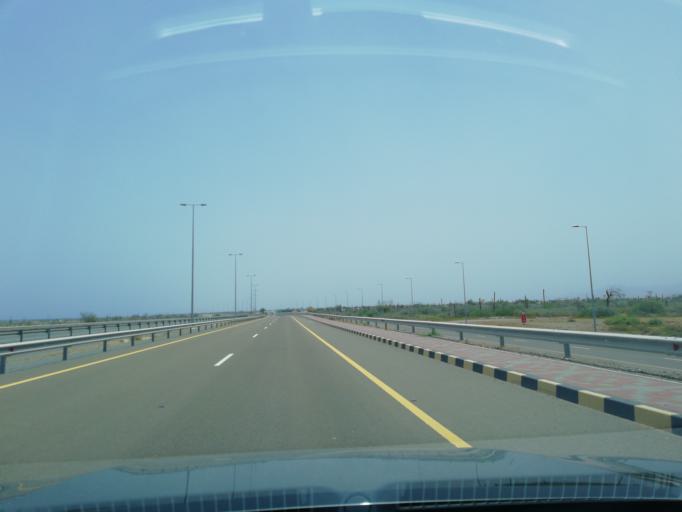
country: OM
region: Al Batinah
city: Shinas
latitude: 24.8783
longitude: 56.4048
